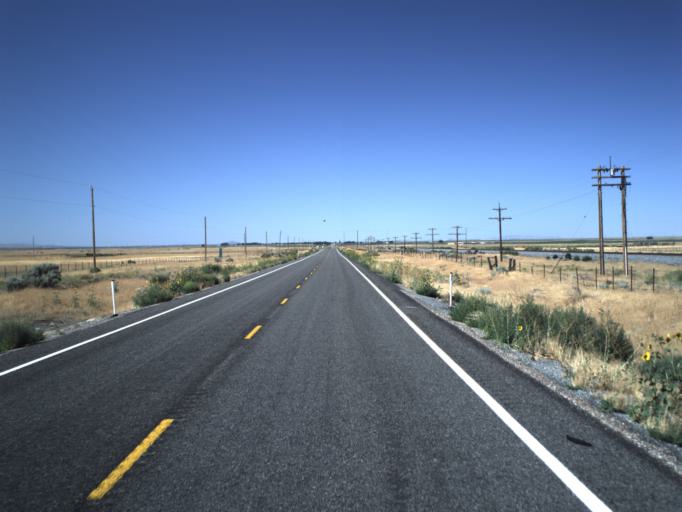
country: US
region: Utah
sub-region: Millard County
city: Delta
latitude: 39.5866
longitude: -112.3329
